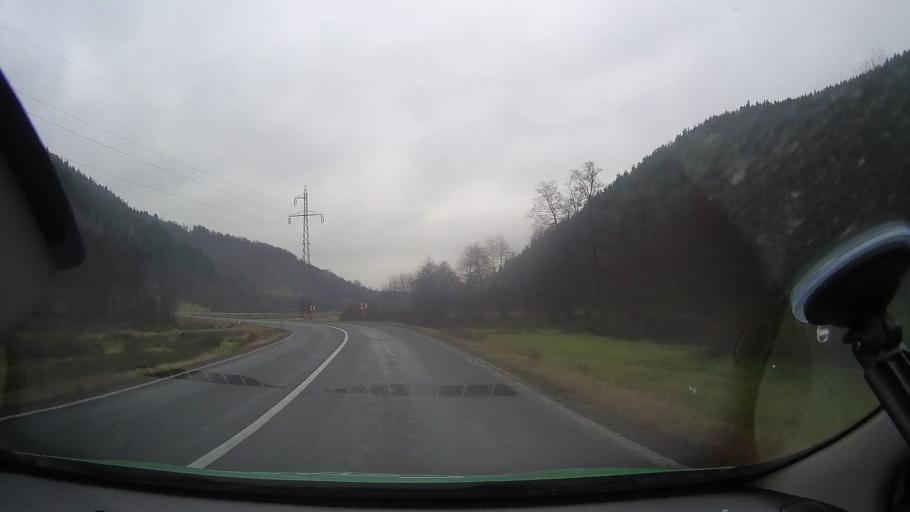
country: RO
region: Arad
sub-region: Comuna Varfurile
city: Varfurile
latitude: 46.3183
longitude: 22.4736
